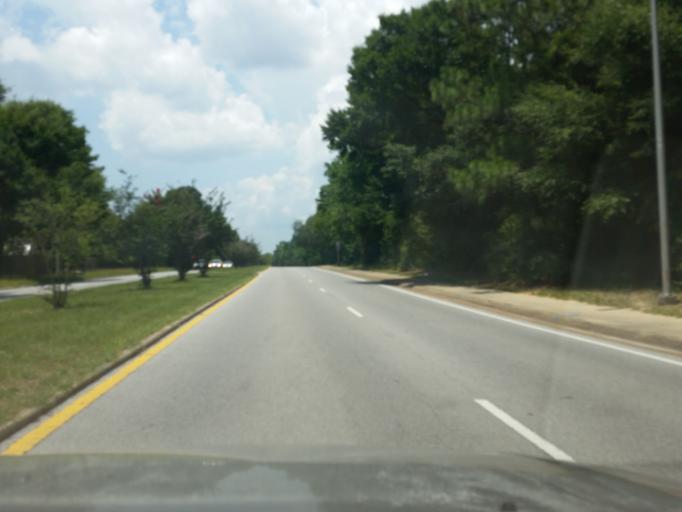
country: US
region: Florida
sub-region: Escambia County
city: East Pensacola Heights
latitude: 30.4588
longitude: -87.1874
